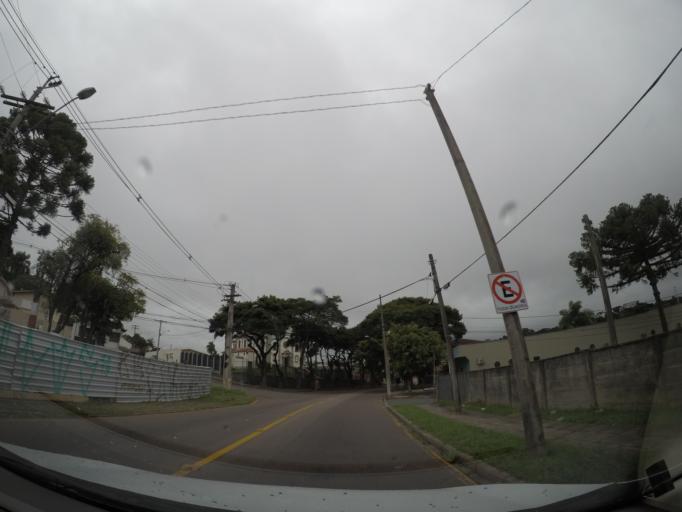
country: BR
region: Parana
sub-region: Curitiba
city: Curitiba
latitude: -25.4489
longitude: -49.3125
